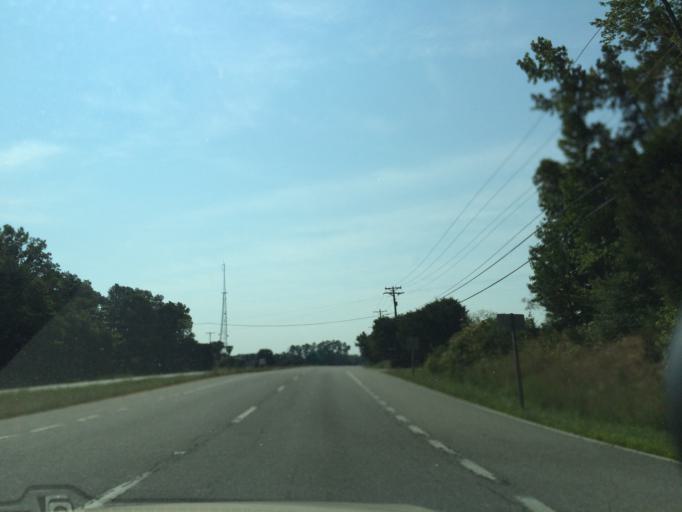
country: US
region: Maryland
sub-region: Charles County
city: La Plata
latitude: 38.4155
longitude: -76.9582
